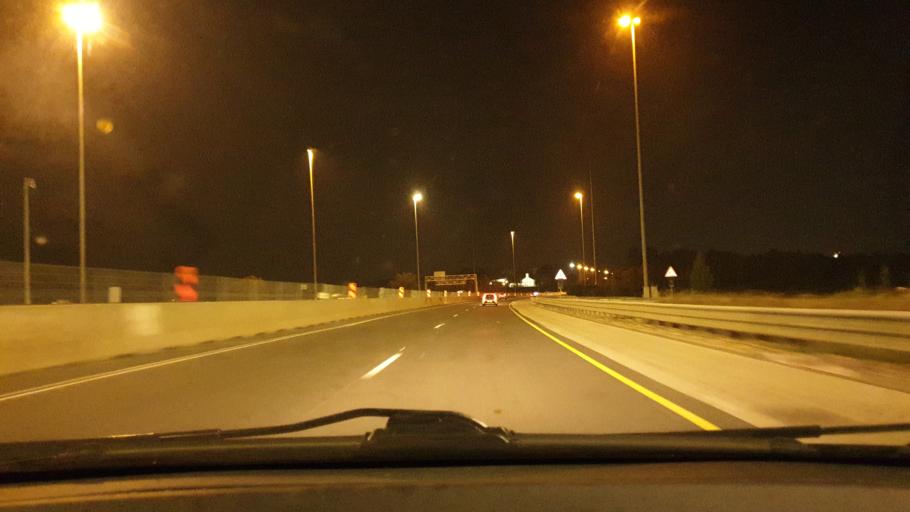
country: IL
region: Central District
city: Ramla
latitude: 31.9219
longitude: 34.8363
